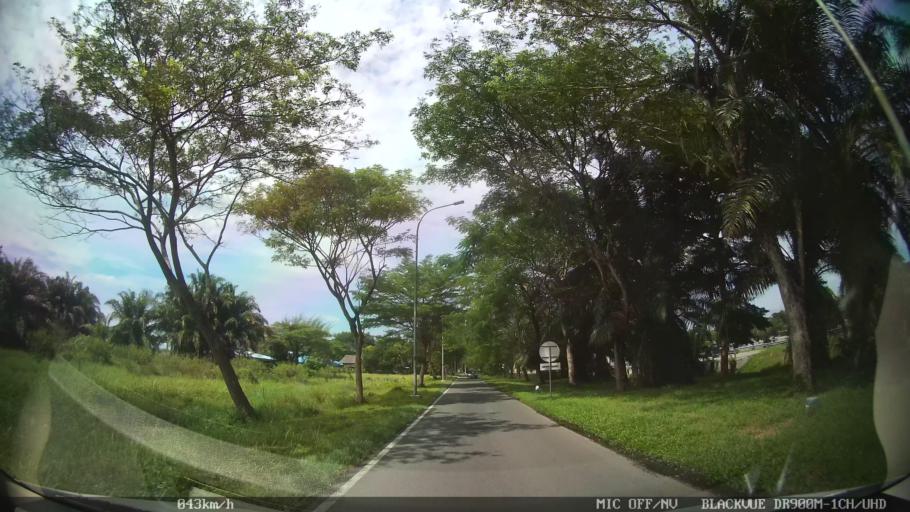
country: ID
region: North Sumatra
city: Percut
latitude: 3.6121
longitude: 98.8565
